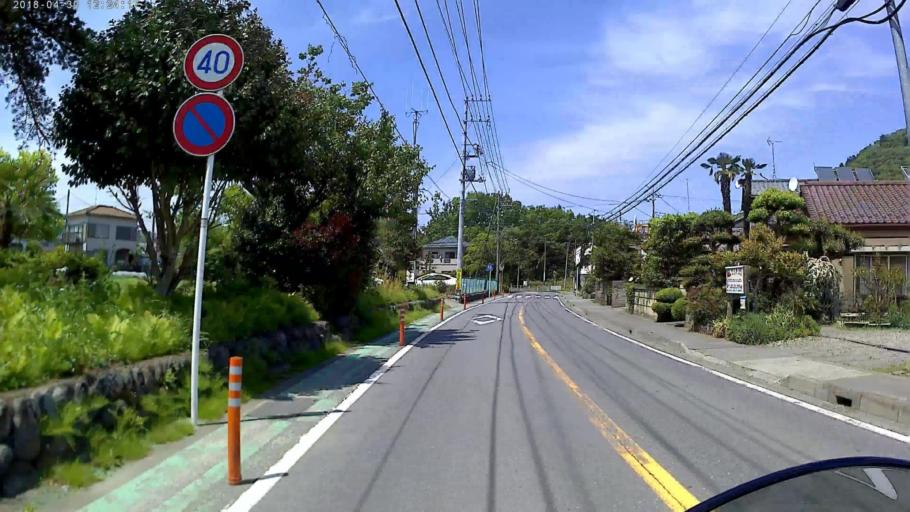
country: JP
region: Tokyo
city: Hachioji
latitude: 35.5762
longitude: 139.2752
